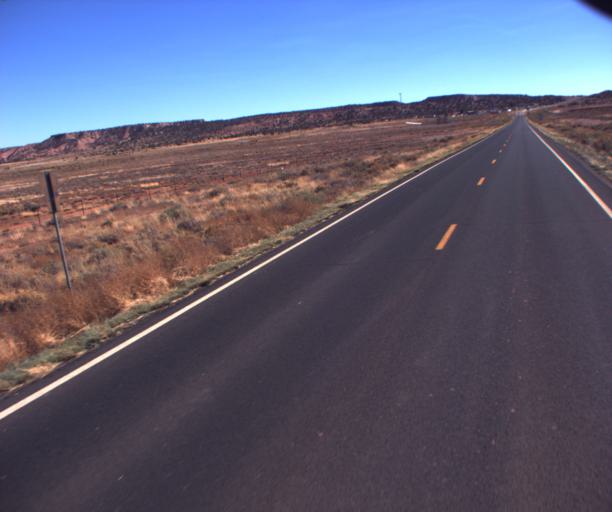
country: US
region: Arizona
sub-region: Apache County
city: Ganado
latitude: 35.7615
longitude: -109.6356
